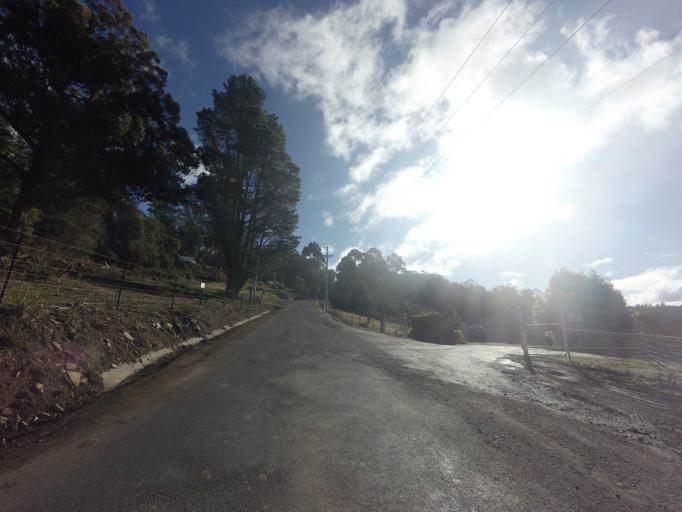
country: AU
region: Tasmania
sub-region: Glenorchy
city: Berriedale
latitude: -42.8398
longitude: 147.1628
